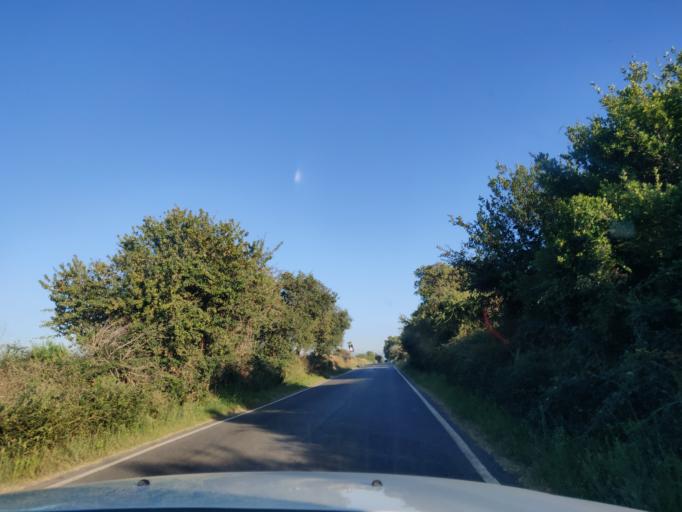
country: IT
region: Latium
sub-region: Provincia di Viterbo
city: Tarquinia
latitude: 42.2709
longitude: 11.6891
